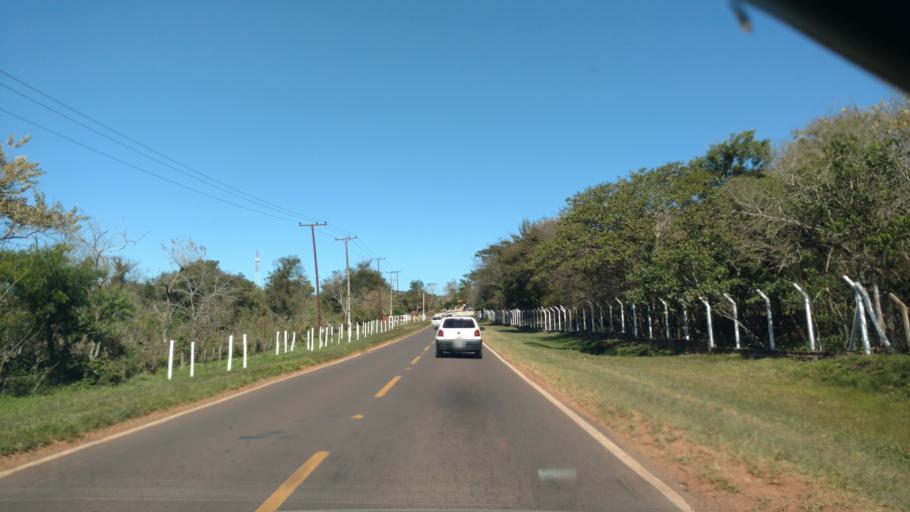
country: PY
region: Paraguari
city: Yaguaron
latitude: -25.5504
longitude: -57.2820
